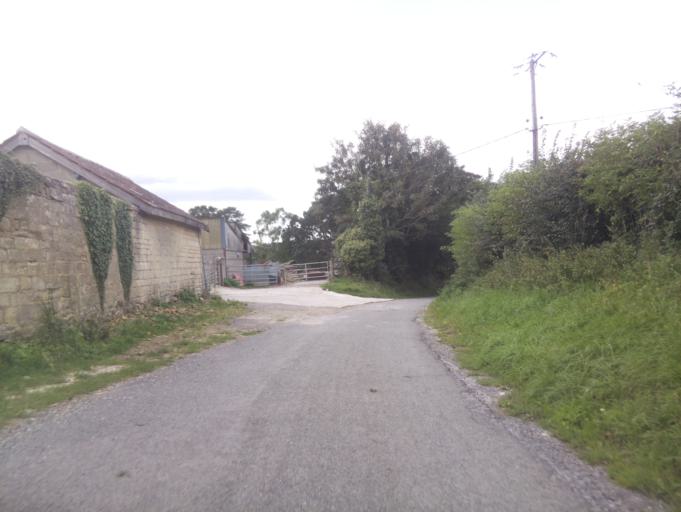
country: GB
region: England
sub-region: Wiltshire
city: Box
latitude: 51.4193
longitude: -2.2599
